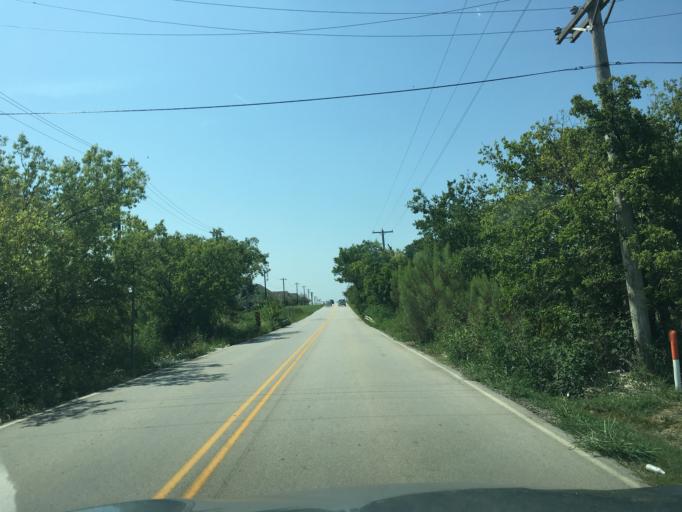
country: US
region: Texas
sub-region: Tarrant County
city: Blue Mound
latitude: 32.9122
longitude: -97.3316
